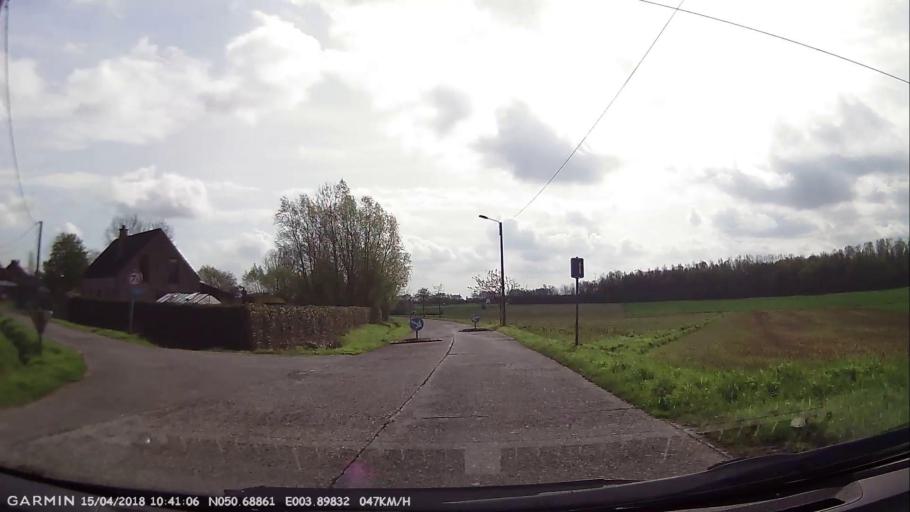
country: BE
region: Wallonia
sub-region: Province du Hainaut
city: Silly
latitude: 50.6886
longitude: 3.8983
